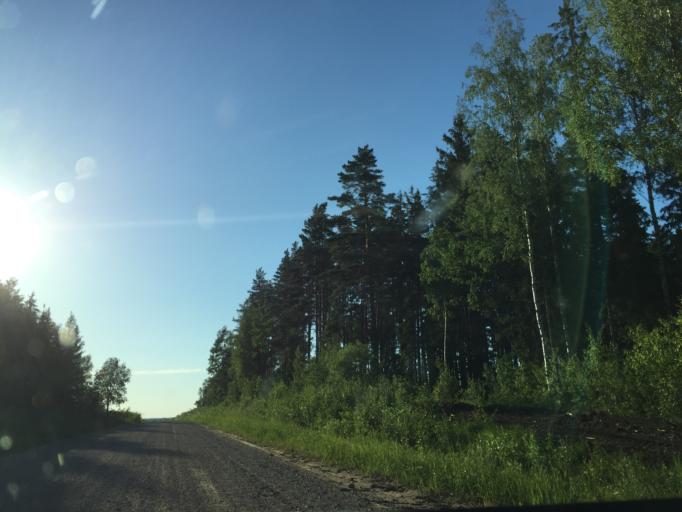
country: LV
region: Talsu Rajons
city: Sabile
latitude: 56.8732
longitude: 22.6234
